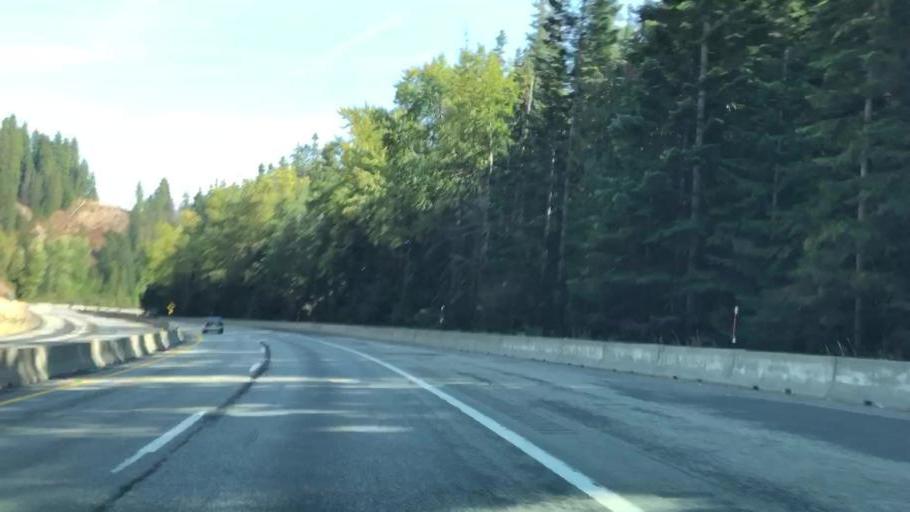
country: US
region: Idaho
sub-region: Kootenai County
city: Coeur d'Alene
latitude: 47.6108
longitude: -116.5190
